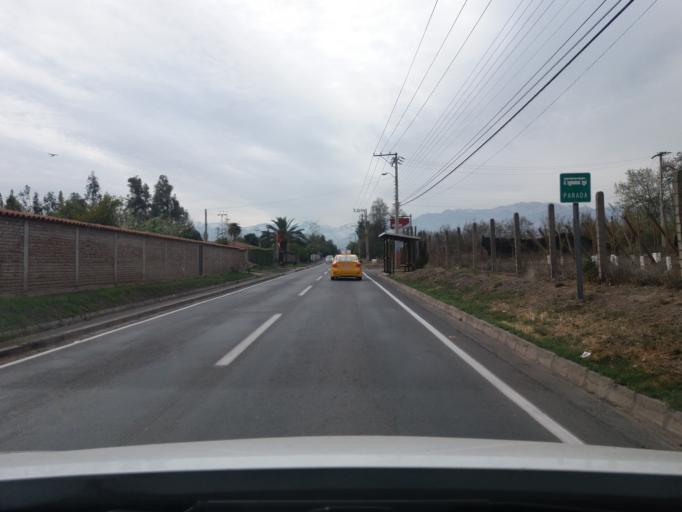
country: CL
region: Valparaiso
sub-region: Provincia de Los Andes
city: Los Andes
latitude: -32.8231
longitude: -70.6670
